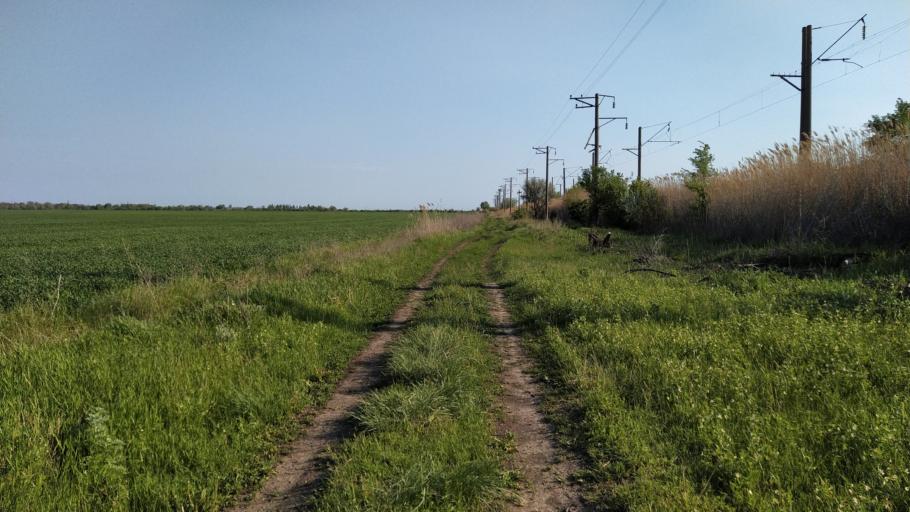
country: RU
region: Rostov
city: Bataysk
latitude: 47.1177
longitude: 39.7138
